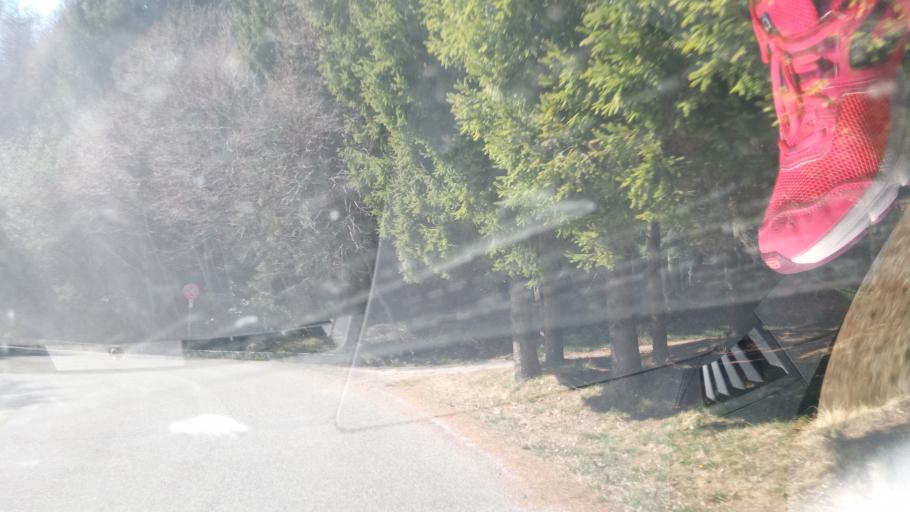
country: IT
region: Veneto
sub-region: Provincia di Treviso
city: Borso del Grappa
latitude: 45.8249
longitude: 11.7706
